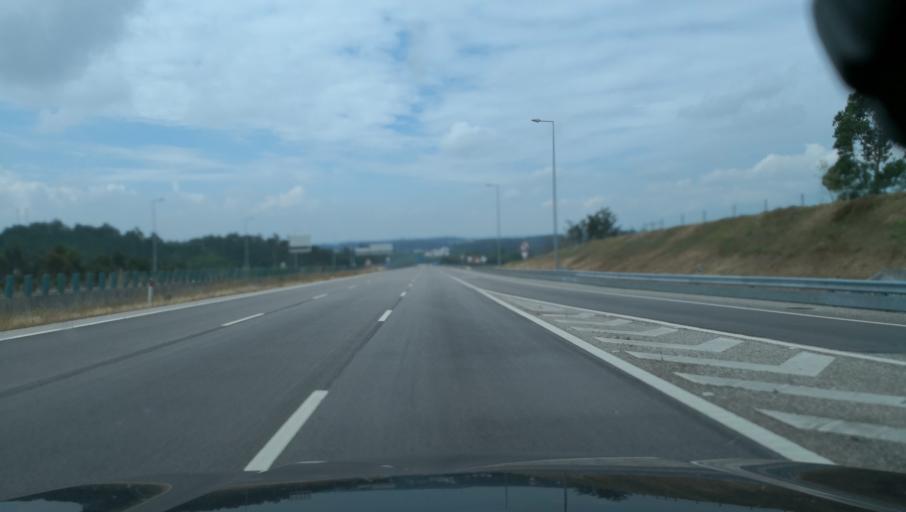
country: PT
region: Leiria
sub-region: Leiria
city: Souto da Carpalhosa
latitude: 39.8512
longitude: -8.8302
